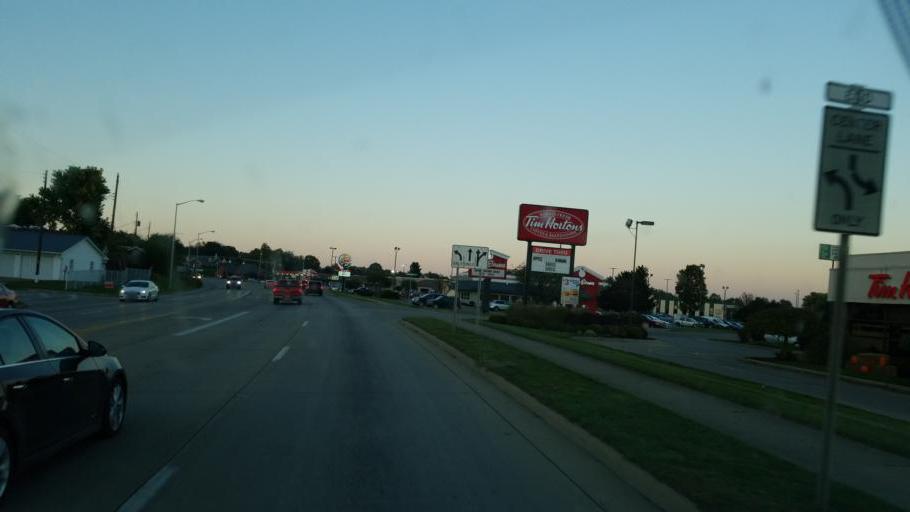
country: US
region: Ohio
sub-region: Pike County
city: Waverly
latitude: 39.1313
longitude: -82.9795
